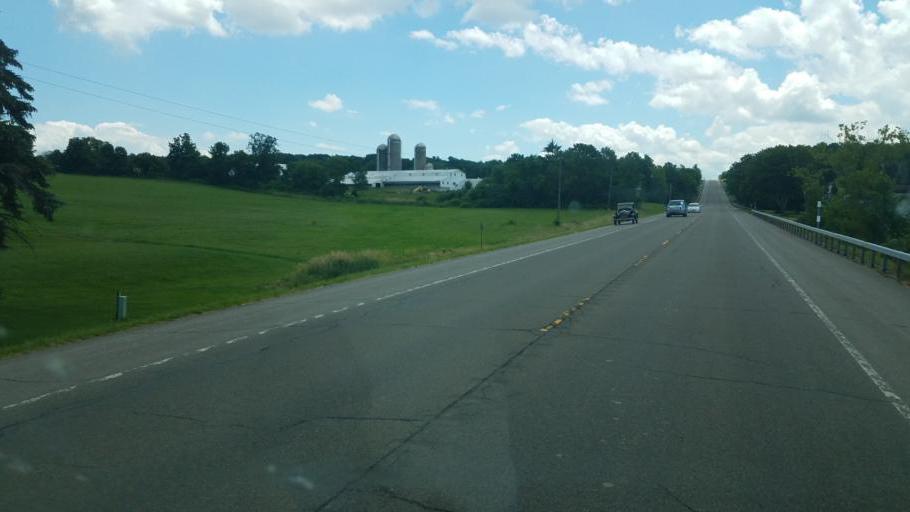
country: US
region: New York
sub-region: Yates County
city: Keuka Park
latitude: 42.5985
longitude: -77.0375
